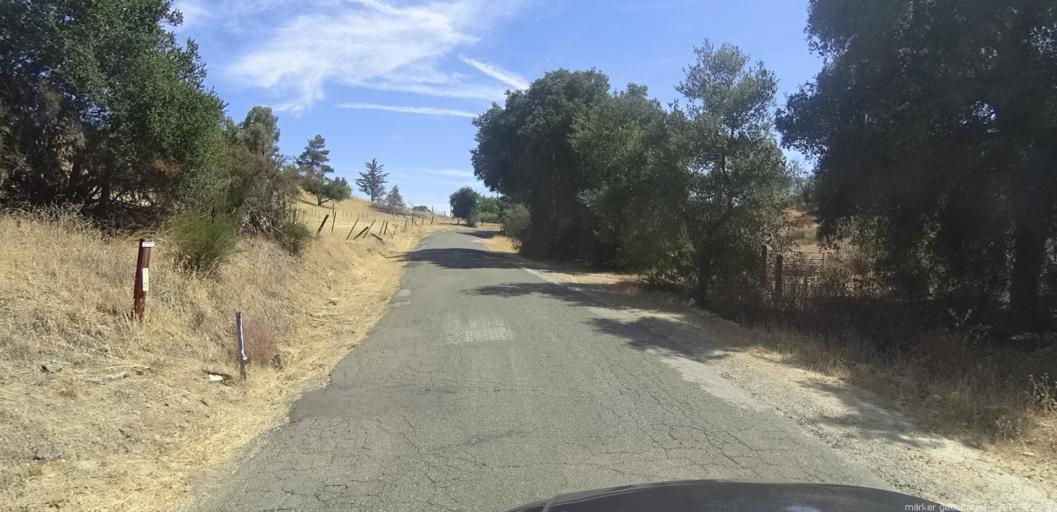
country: US
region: California
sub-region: San Luis Obispo County
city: Lake Nacimiento
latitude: 35.8227
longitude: -121.0589
